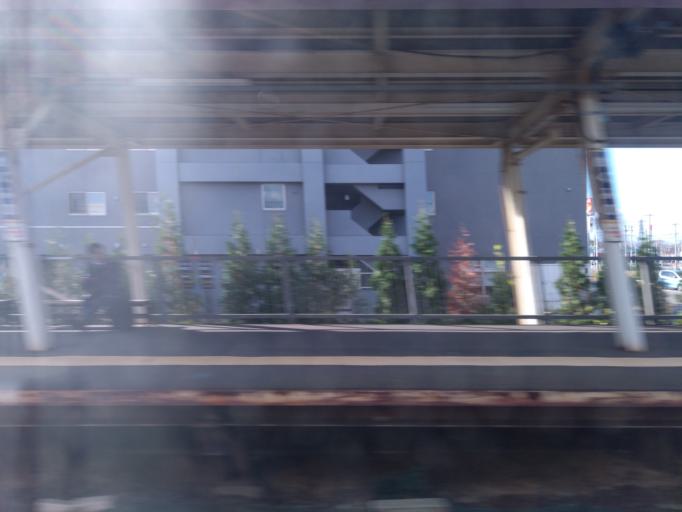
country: JP
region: Hokkaido
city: Kitahiroshima
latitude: 42.9029
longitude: 141.5745
